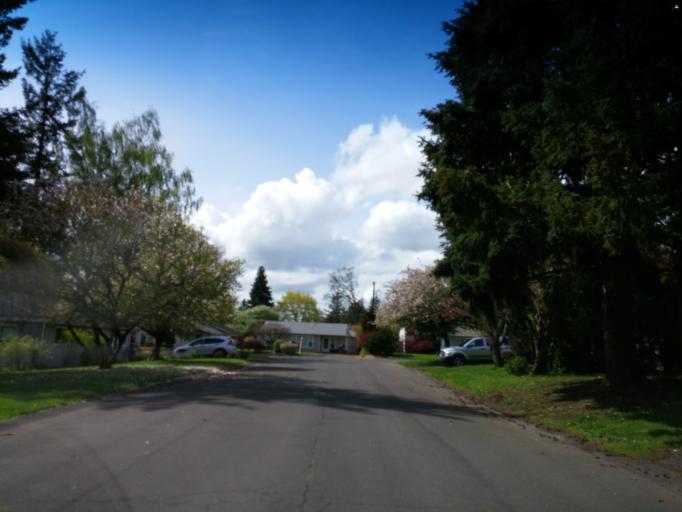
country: US
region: Oregon
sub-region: Washington County
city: Cedar Hills
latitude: 45.5042
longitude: -122.8106
